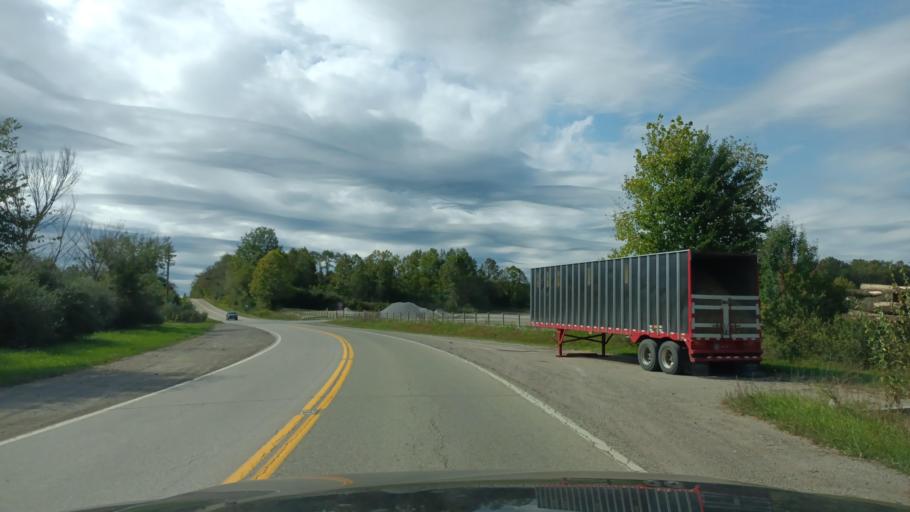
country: US
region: Ohio
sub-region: Athens County
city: Athens
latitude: 39.2117
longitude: -82.2374
